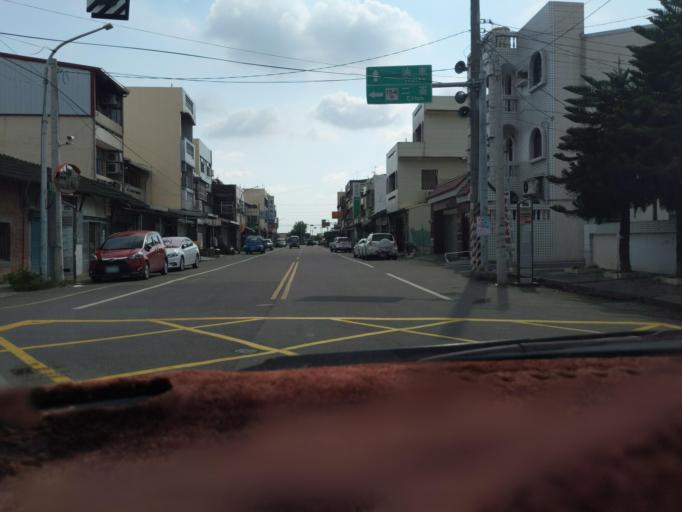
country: TW
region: Taiwan
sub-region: Yunlin
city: Douliu
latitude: 23.7983
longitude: 120.4422
